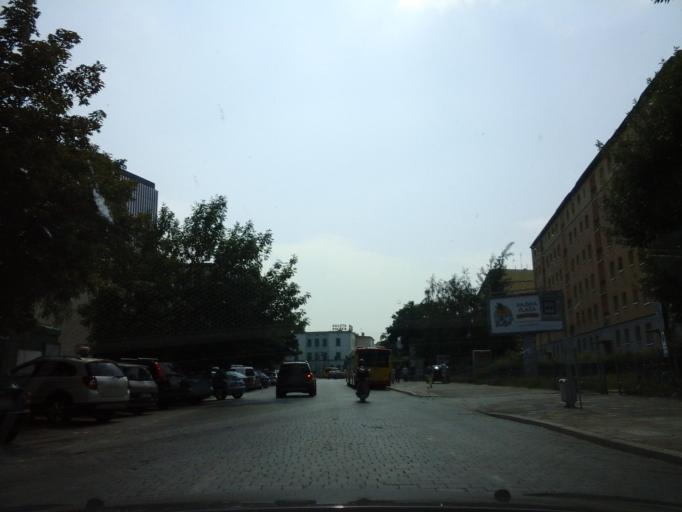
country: PL
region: Lower Silesian Voivodeship
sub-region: Powiat wroclawski
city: Wroclaw
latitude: 51.1011
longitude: 17.0396
